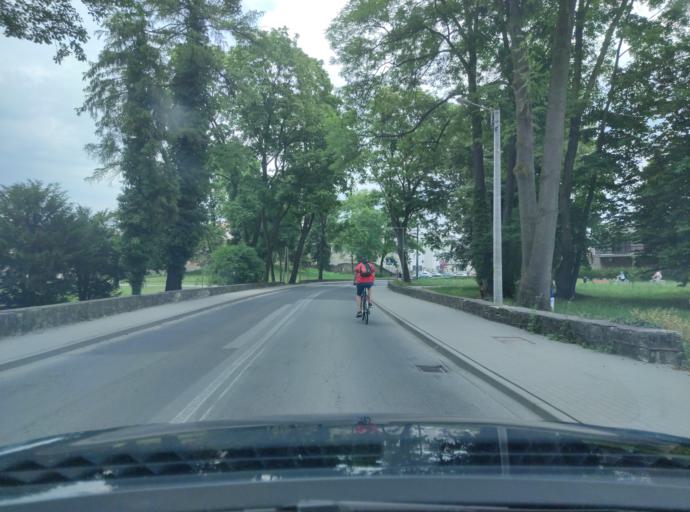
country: PL
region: Opole Voivodeship
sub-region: Powiat strzelecki
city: Strzelce Opolskie
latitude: 50.5086
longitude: 18.3006
